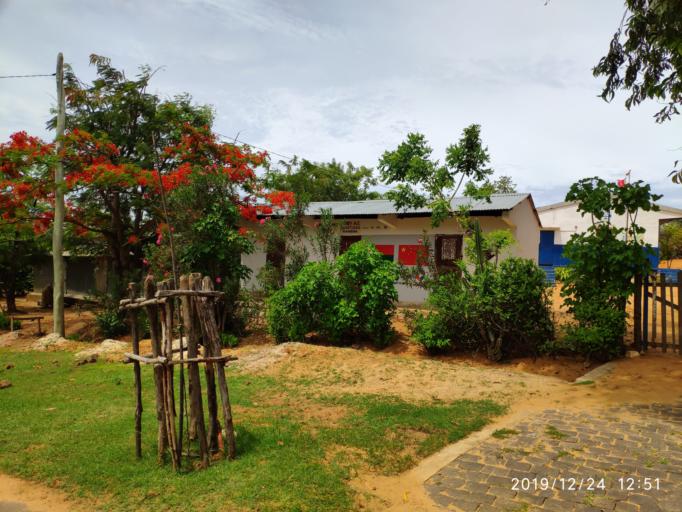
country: MG
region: Diana
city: Antsiranana
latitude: -12.2435
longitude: 49.3469
